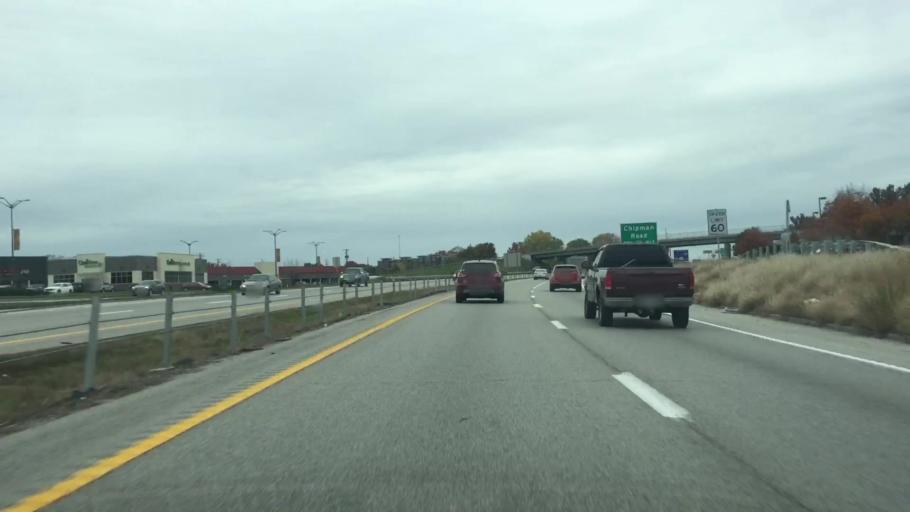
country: US
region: Missouri
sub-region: Jackson County
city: Lees Summit
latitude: 38.9167
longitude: -94.4001
